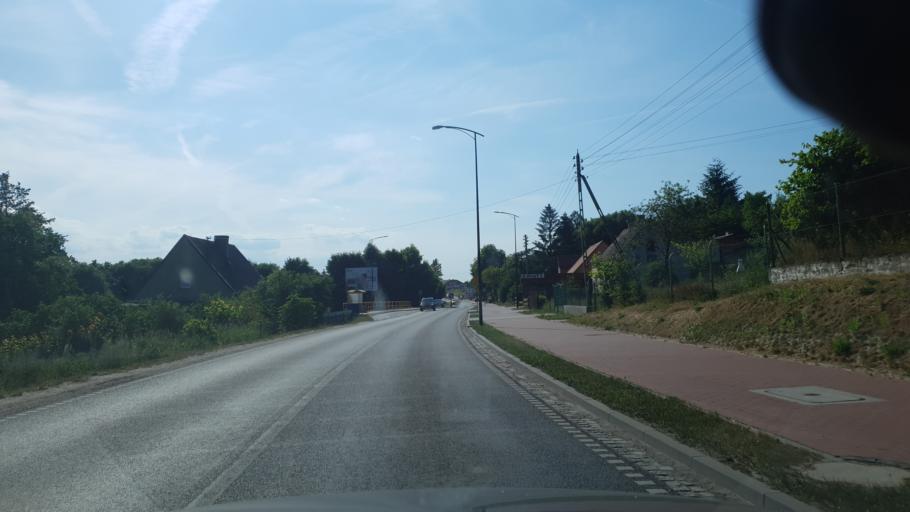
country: PL
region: Pomeranian Voivodeship
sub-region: Powiat kartuski
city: Chwaszczyno
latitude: 54.4420
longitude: 18.4474
